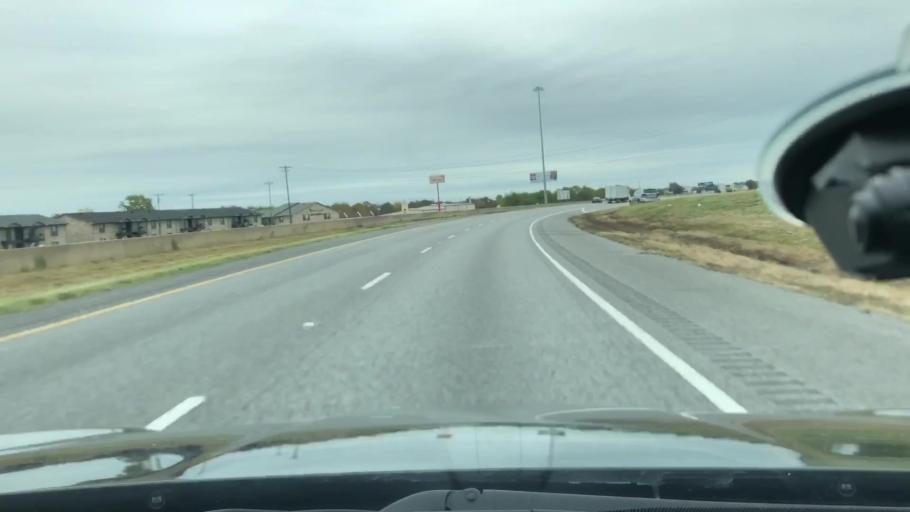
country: US
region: Texas
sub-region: Hunt County
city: Greenville
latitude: 33.1201
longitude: -96.0958
